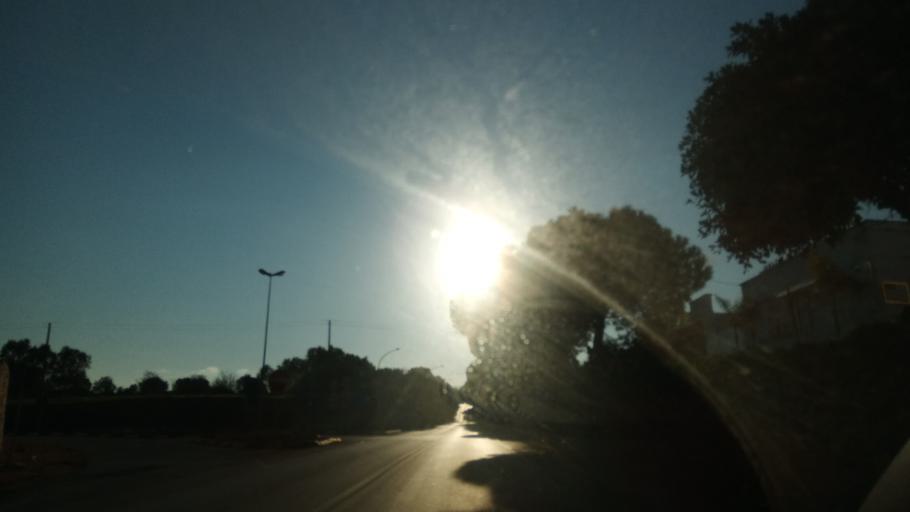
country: IT
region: Apulia
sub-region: Provincia di Bari
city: Polignano a Mare
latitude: 40.9890
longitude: 17.2148
